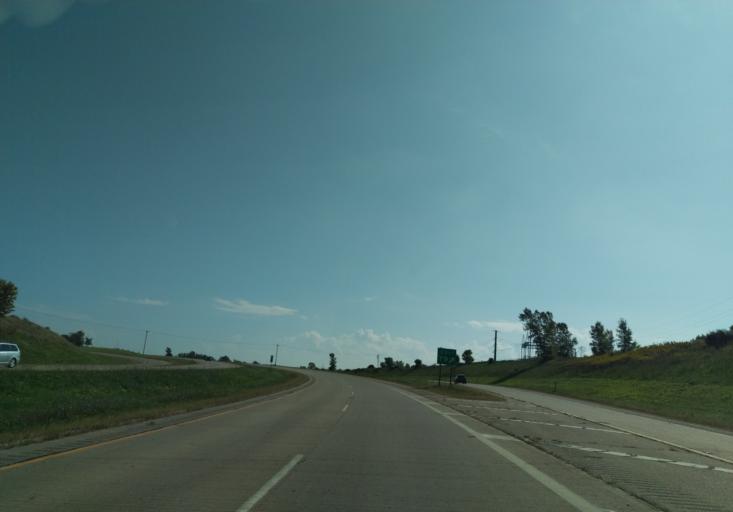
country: US
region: Wisconsin
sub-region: Dane County
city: Verona
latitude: 42.9731
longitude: -89.5186
